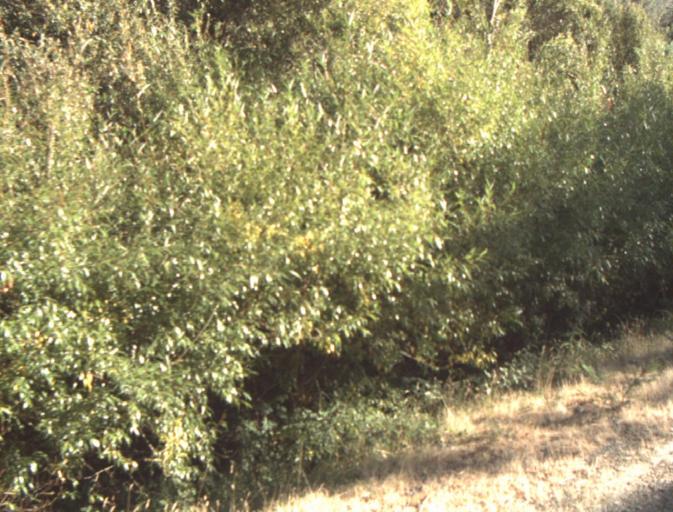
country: AU
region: Tasmania
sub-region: Launceston
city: Newstead
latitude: -41.4191
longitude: 147.2581
